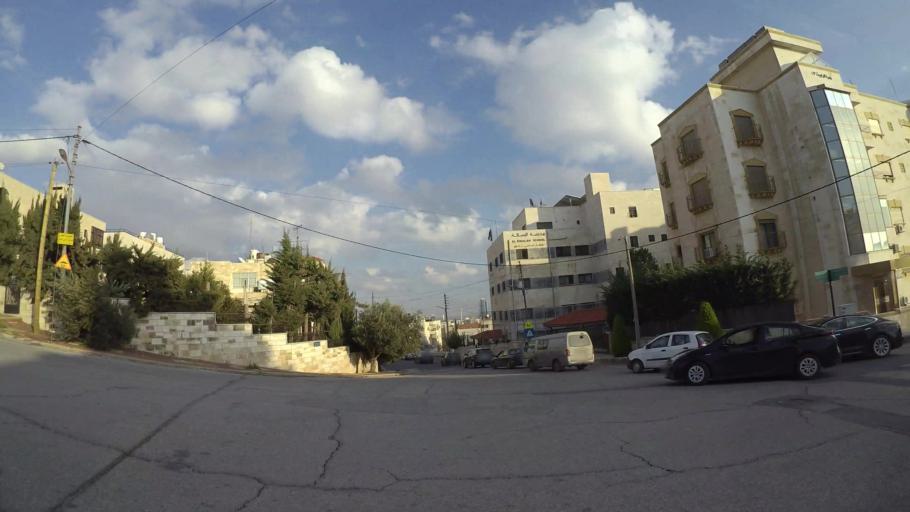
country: JO
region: Amman
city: Al Jubayhah
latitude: 31.9800
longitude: 35.8852
